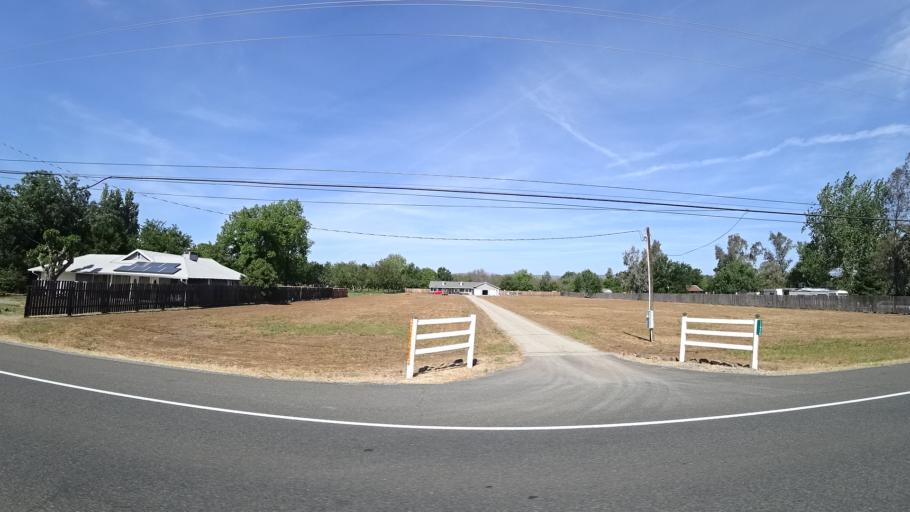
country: US
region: California
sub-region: Tehama County
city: Gerber
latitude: 40.1401
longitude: -122.1308
